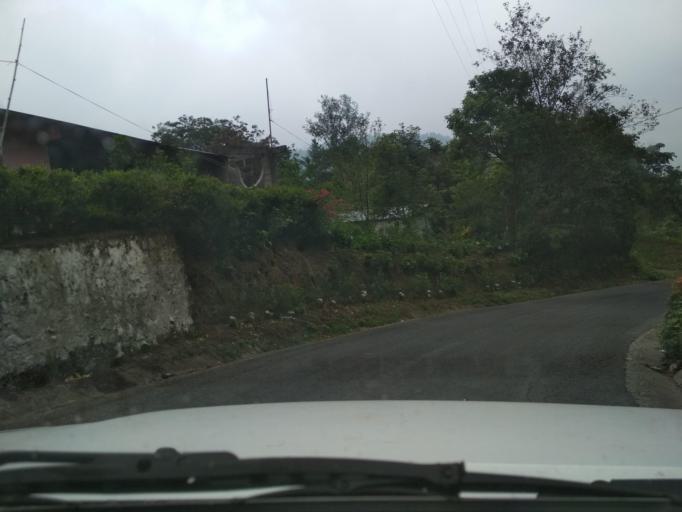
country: MX
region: Veracruz
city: La Perla
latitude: 18.9377
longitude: -97.1442
